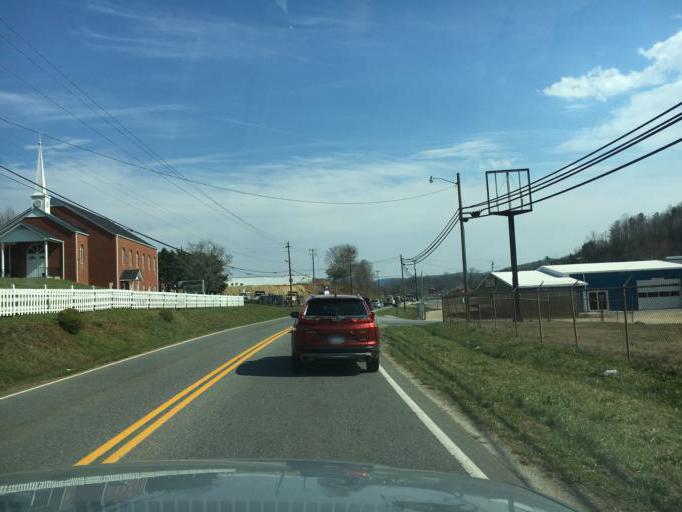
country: US
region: North Carolina
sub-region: McDowell County
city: Marion
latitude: 35.6714
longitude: -81.9863
